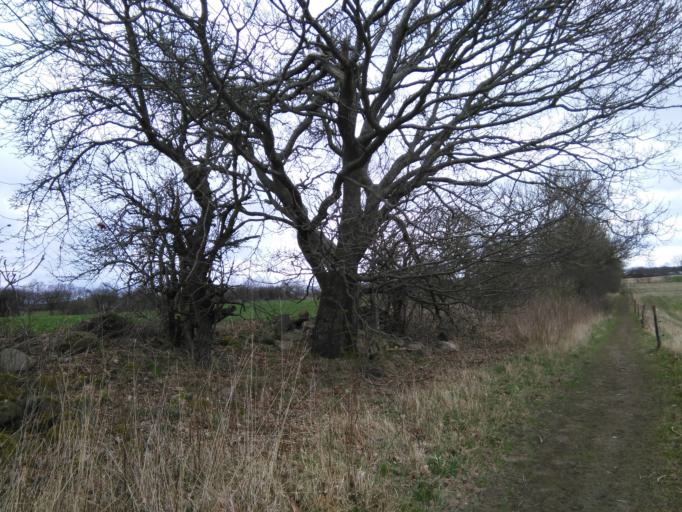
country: DK
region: Central Jutland
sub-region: Arhus Kommune
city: Beder
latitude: 56.0494
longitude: 10.2050
